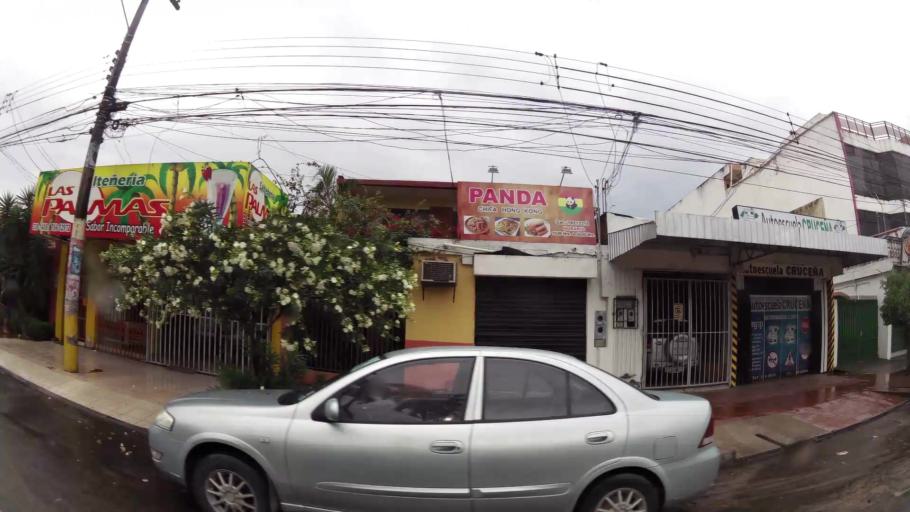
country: BO
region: Santa Cruz
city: Santa Cruz de la Sierra
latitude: -17.7972
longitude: -63.1746
